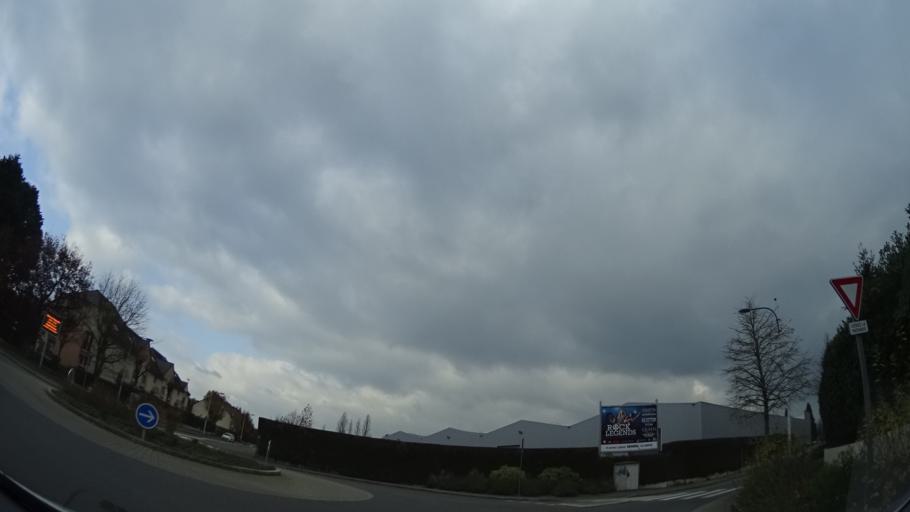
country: FR
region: Brittany
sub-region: Departement d'Ille-et-Vilaine
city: Montgermont
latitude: 48.1550
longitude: -1.7105
